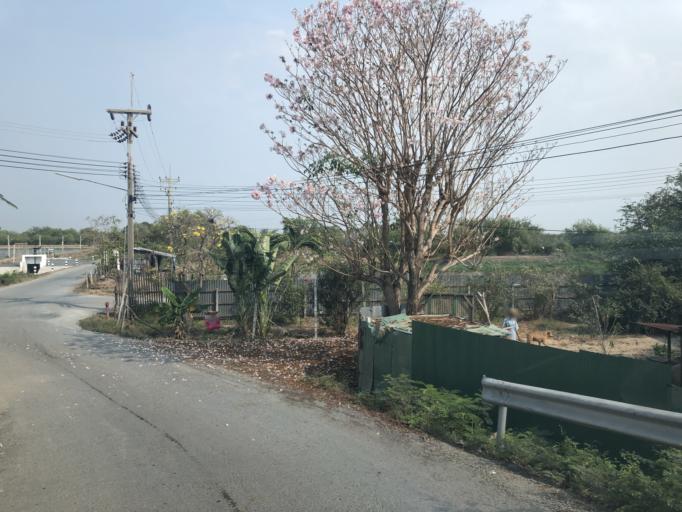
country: TH
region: Chachoengsao
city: Bang Pakong
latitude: 13.5114
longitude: 100.9264
